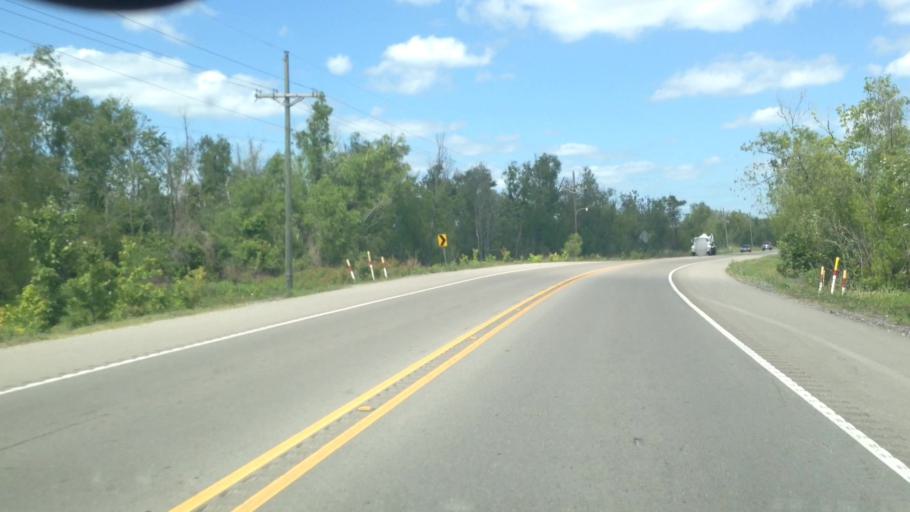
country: US
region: Louisiana
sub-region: Terrebonne Parish
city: Houma
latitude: 29.6340
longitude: -90.7016
